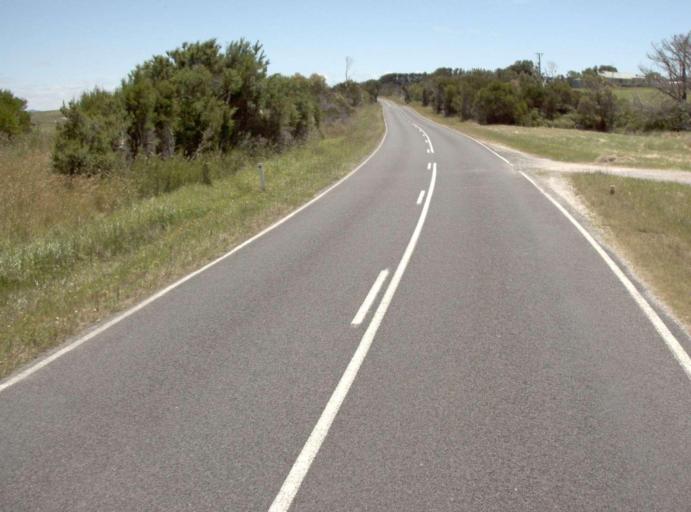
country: AU
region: Victoria
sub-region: Latrobe
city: Morwell
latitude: -38.8411
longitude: 146.2422
